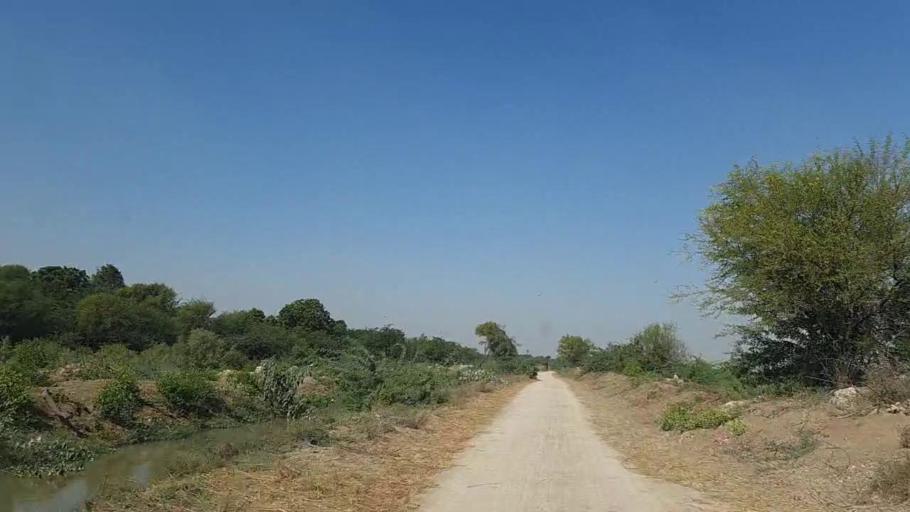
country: PK
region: Sindh
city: Daro Mehar
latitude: 24.7622
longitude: 68.1572
